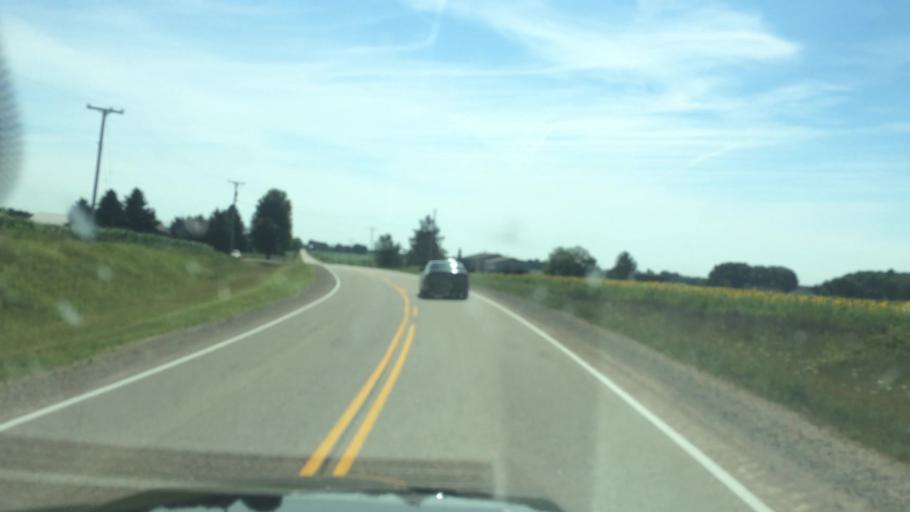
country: US
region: Wisconsin
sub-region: Shawano County
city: Bonduel
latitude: 44.7872
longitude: -88.3494
